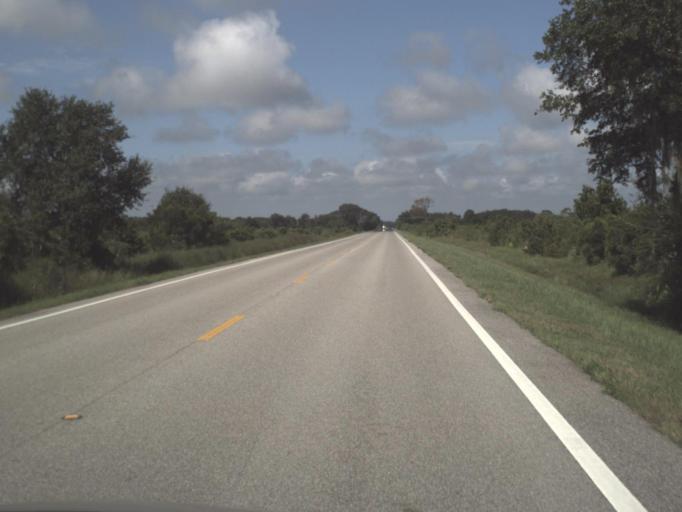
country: US
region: Florida
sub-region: Sarasota County
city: Warm Mineral Springs
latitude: 27.2171
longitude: -82.2740
